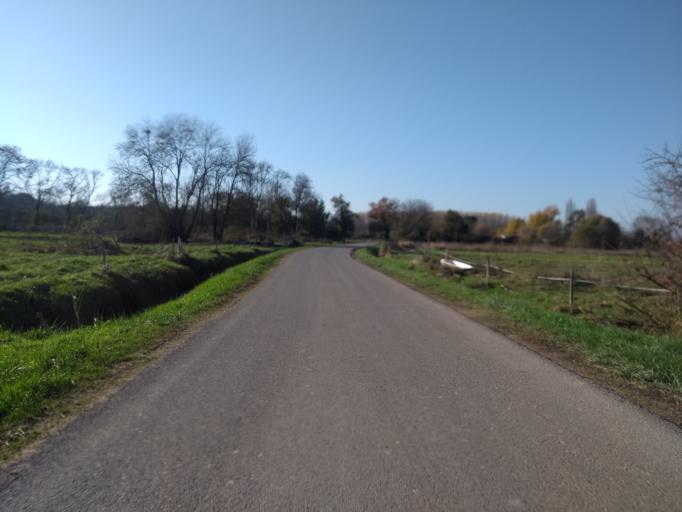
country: FR
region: Aquitaine
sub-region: Departement de la Gironde
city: Cambes
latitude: 44.7196
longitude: -0.4644
